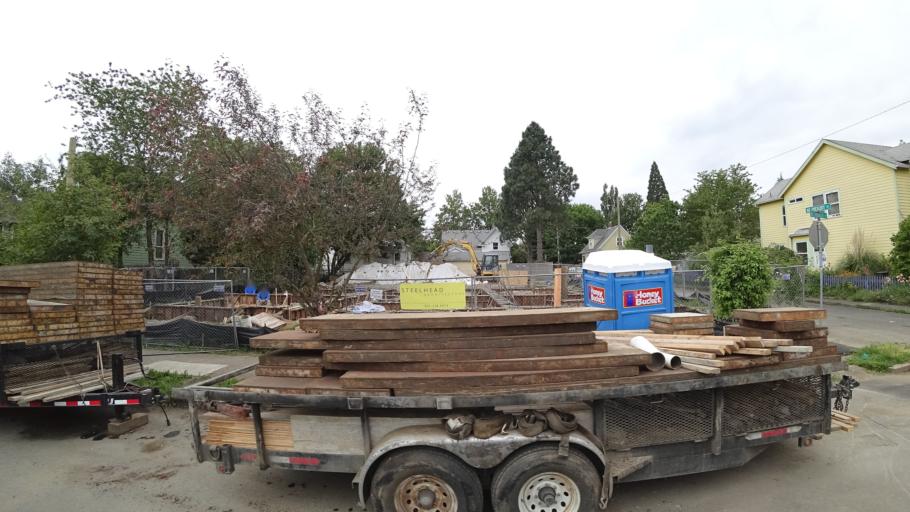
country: US
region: Oregon
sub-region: Multnomah County
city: Portland
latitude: 45.5555
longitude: -122.6647
